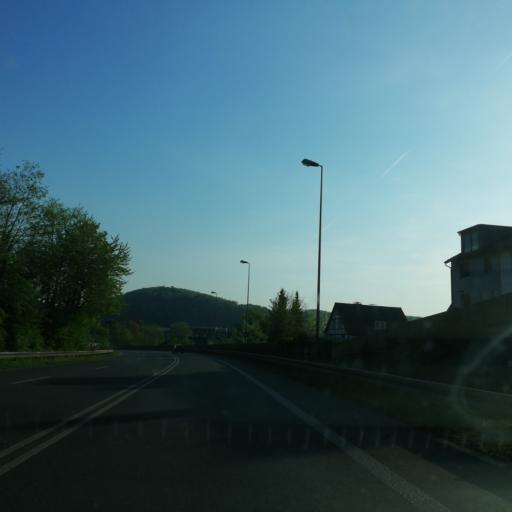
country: DE
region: North Rhine-Westphalia
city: Herdecke
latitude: 51.3988
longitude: 7.4344
